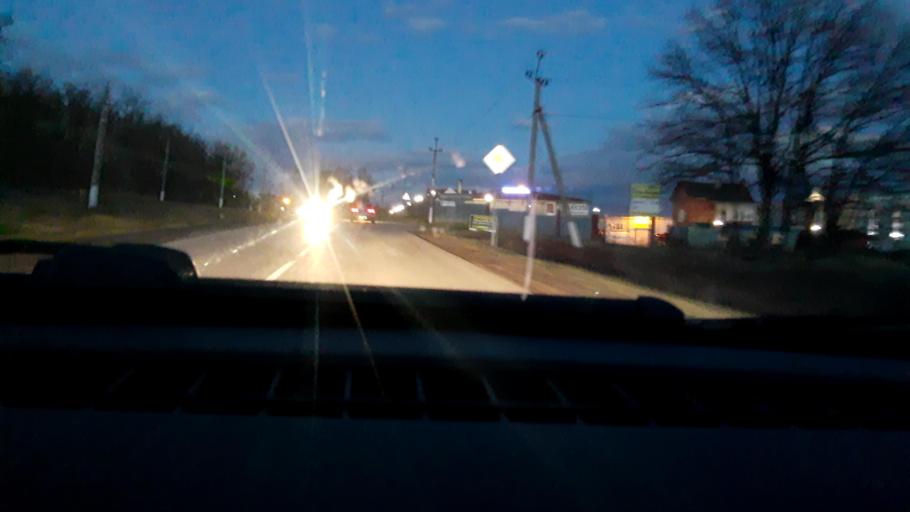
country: RU
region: Bashkortostan
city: Mikhaylovka
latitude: 54.8061
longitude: 55.8764
